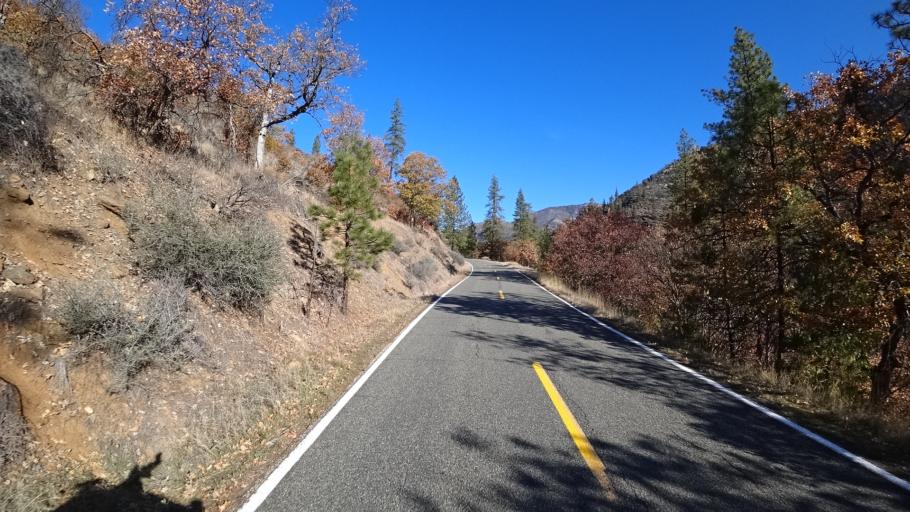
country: US
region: California
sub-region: Siskiyou County
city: Yreka
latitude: 41.8811
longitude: -122.8221
